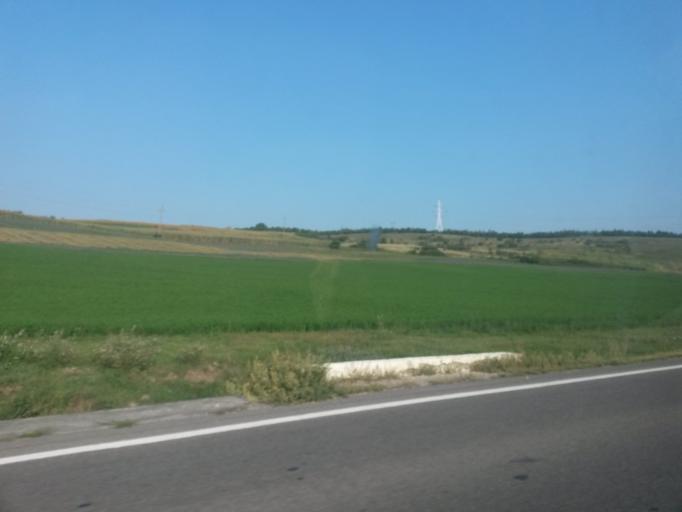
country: RO
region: Alba
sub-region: Comuna Unirea
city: Unirea
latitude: 46.4177
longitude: 23.8050
